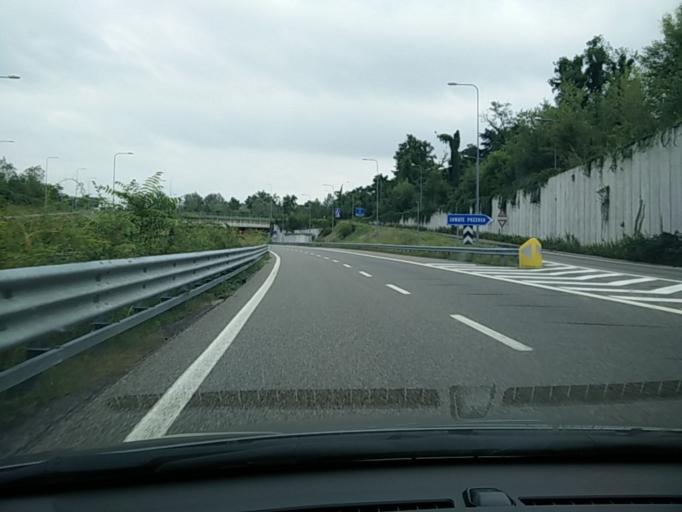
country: IT
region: Lombardy
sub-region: Provincia di Varese
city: Lonate Pozzolo
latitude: 45.5723
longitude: 8.7405
